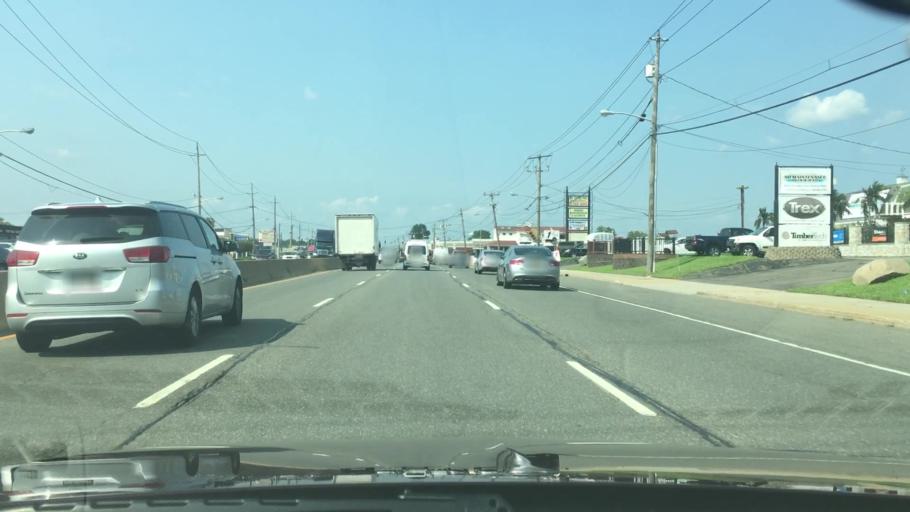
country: US
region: New York
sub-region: Suffolk County
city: East Farmingdale
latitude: 40.7403
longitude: -73.4230
